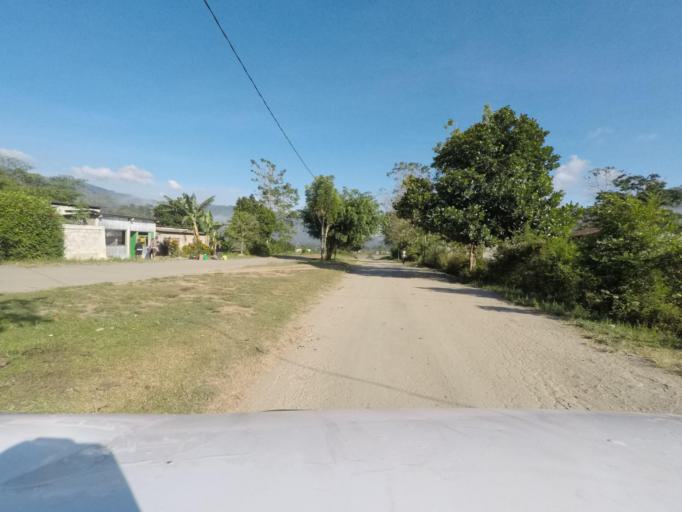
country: TL
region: Ermera
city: Gleno
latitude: -8.7220
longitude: 125.4285
